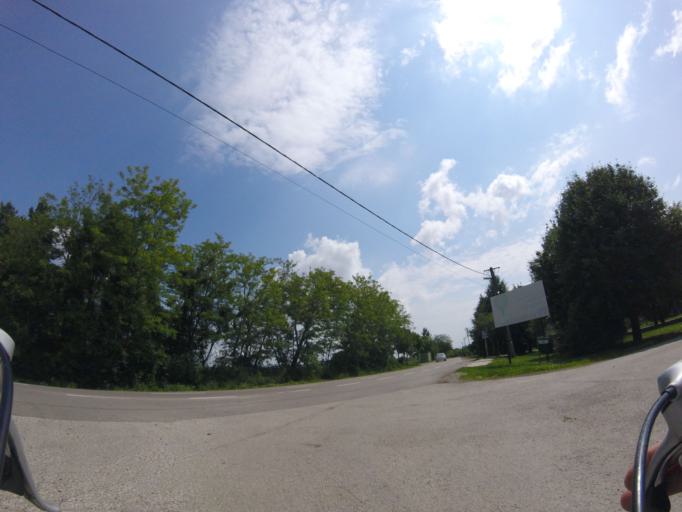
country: HU
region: Baranya
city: Kozarmisleny
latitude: 46.0723
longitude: 18.3120
